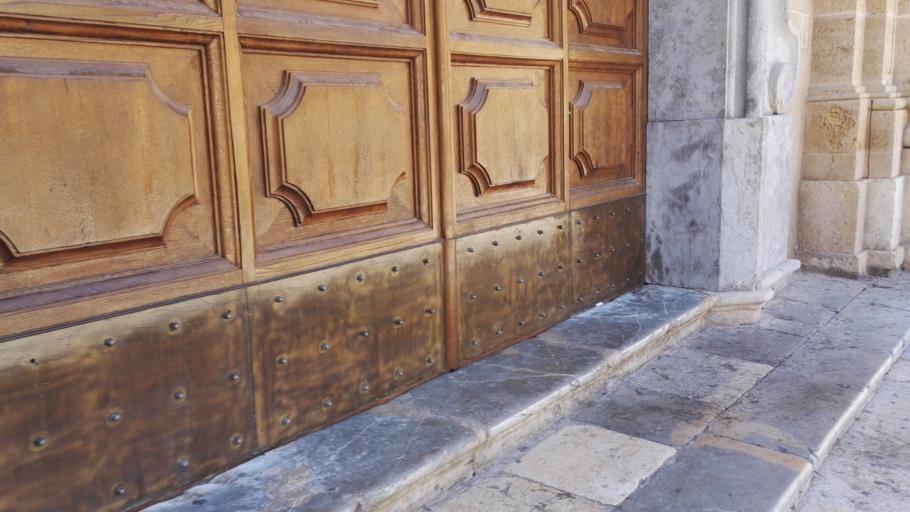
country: IT
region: Sicily
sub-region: Trapani
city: Marsala
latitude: 37.7993
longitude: 12.4345
